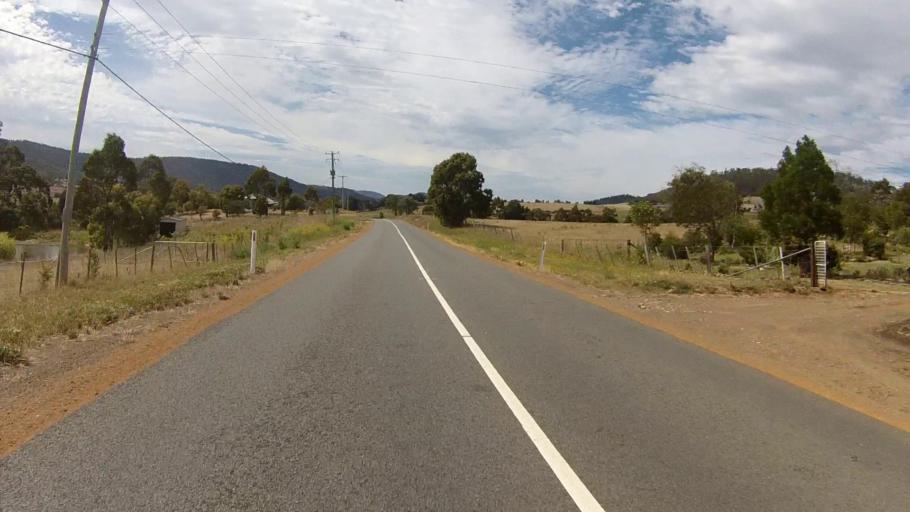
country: AU
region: Tasmania
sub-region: Brighton
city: Old Beach
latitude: -42.6986
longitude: 147.3558
